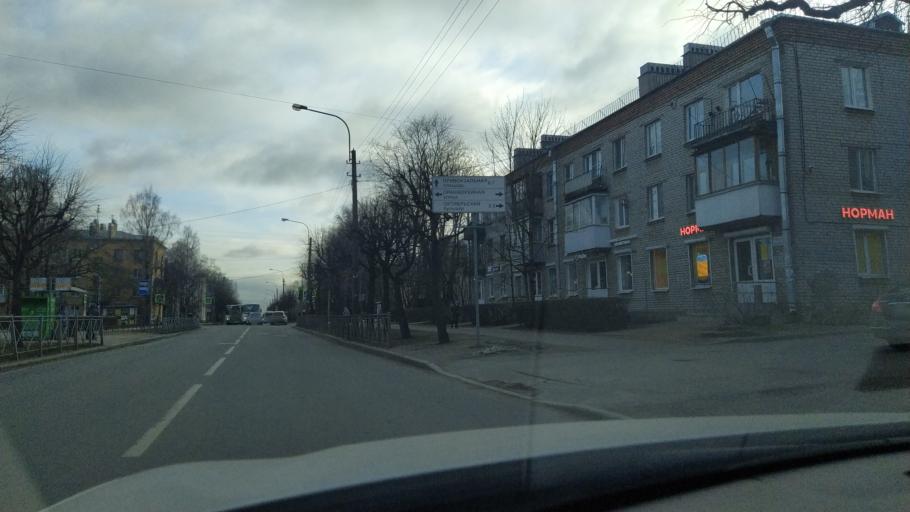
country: RU
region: St.-Petersburg
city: Pushkin
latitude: 59.7271
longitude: 30.4162
